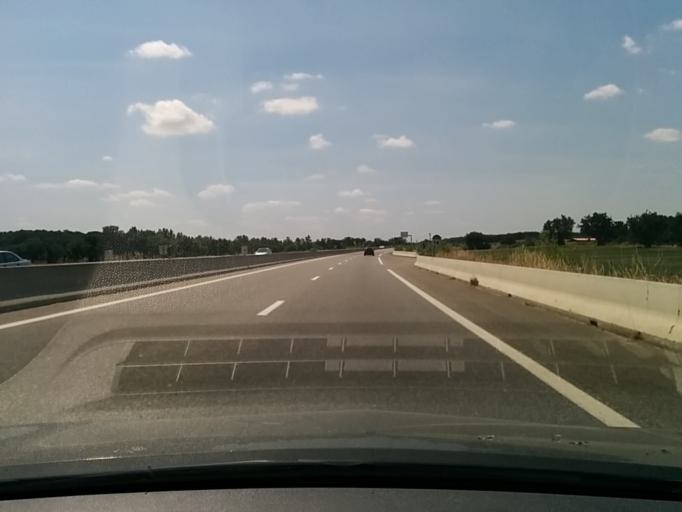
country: FR
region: Midi-Pyrenees
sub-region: Departement de la Haute-Garonne
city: La Salvetat-Saint-Gilles
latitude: 43.5920
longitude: 1.2751
